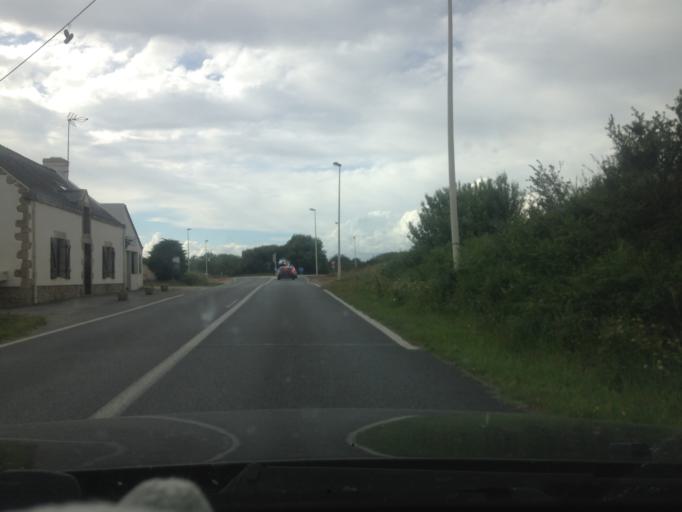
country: FR
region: Brittany
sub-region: Departement du Morbihan
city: Plouharnel
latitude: 47.6194
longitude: -3.1340
